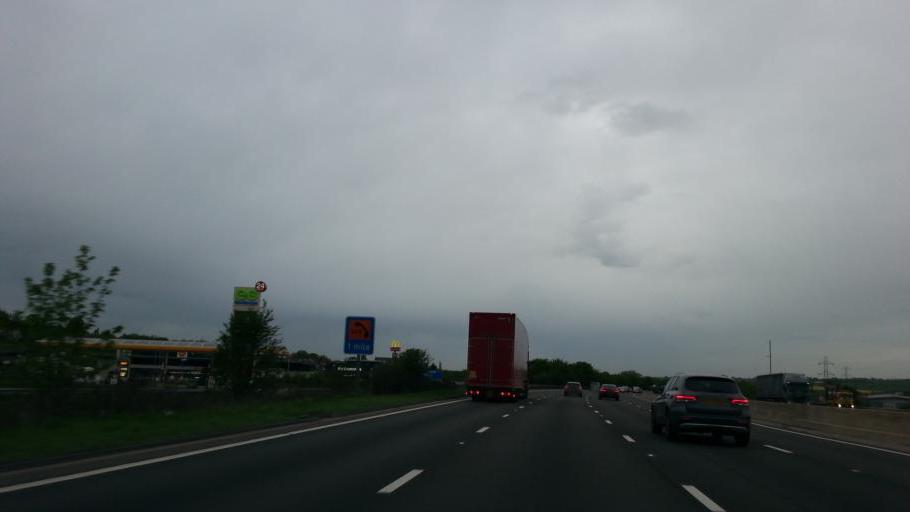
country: GB
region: England
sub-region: Derbyshire
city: Staveley
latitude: 53.2422
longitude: -1.3327
